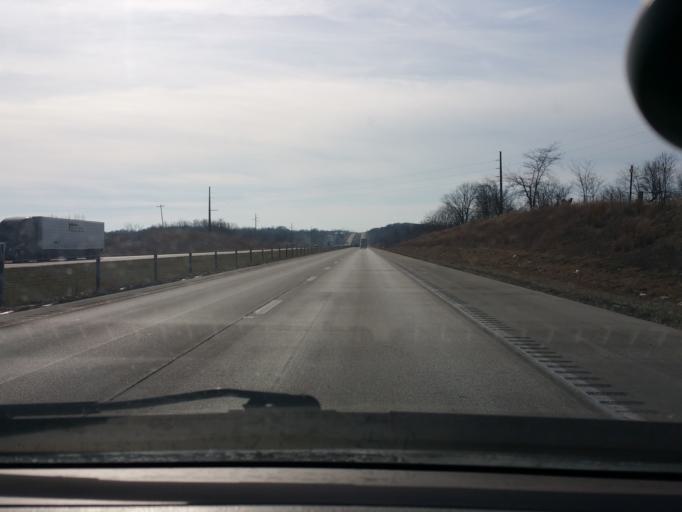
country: US
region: Missouri
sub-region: Clay County
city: Kearney
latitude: 39.3572
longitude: -94.3782
